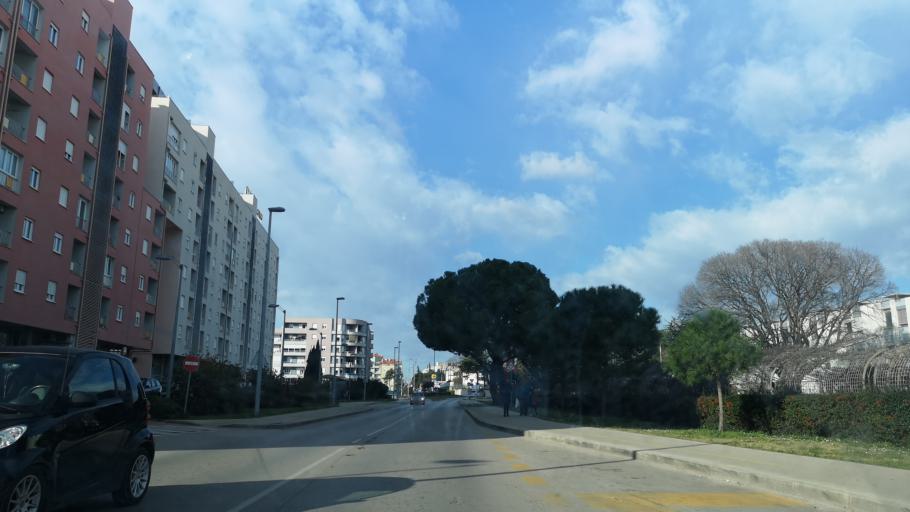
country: HR
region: Zadarska
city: Zadar
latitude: 44.1213
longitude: 15.2389
